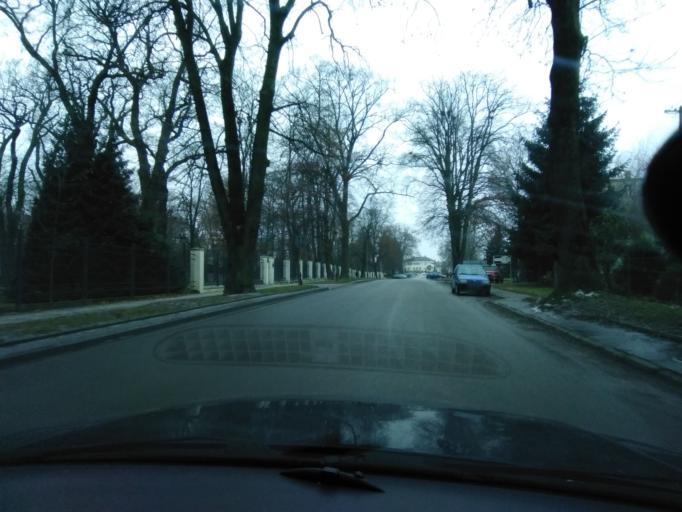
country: PL
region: Subcarpathian Voivodeship
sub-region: Powiat przeworski
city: Zarzecze
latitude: 49.9863
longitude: 22.5416
